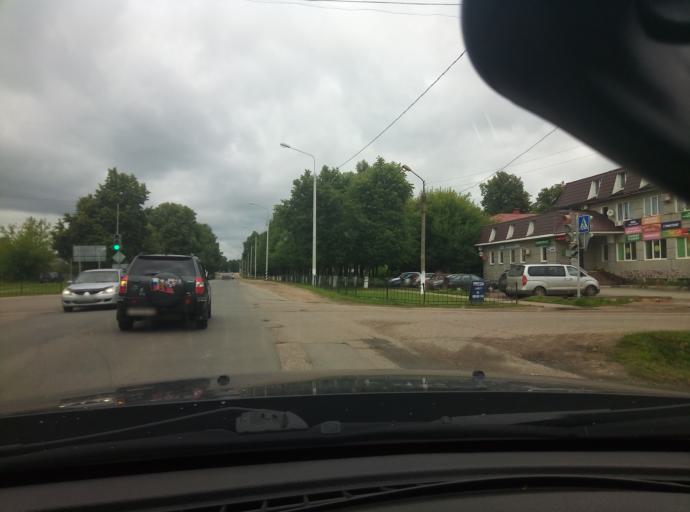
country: RU
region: Kaluga
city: Zhukovo
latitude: 55.0346
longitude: 36.7437
